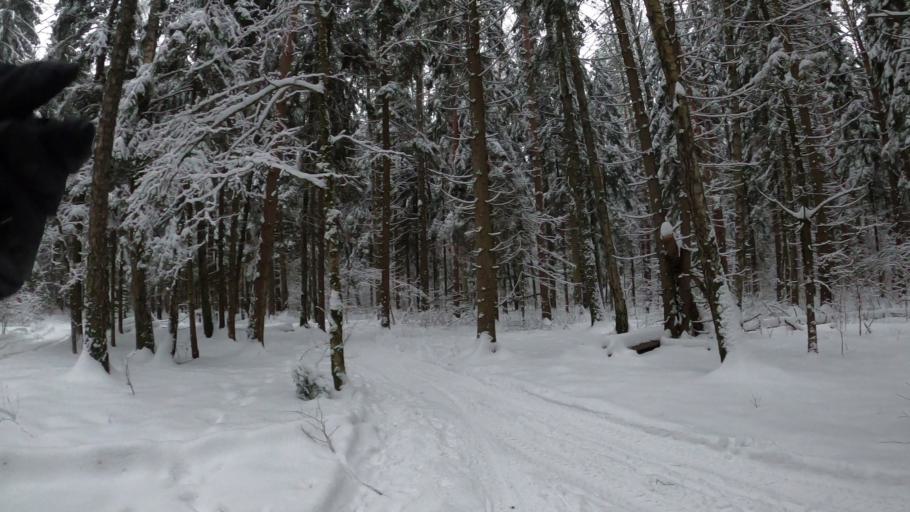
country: RU
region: Moskovskaya
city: Firsanovka
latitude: 55.9311
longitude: 37.2203
